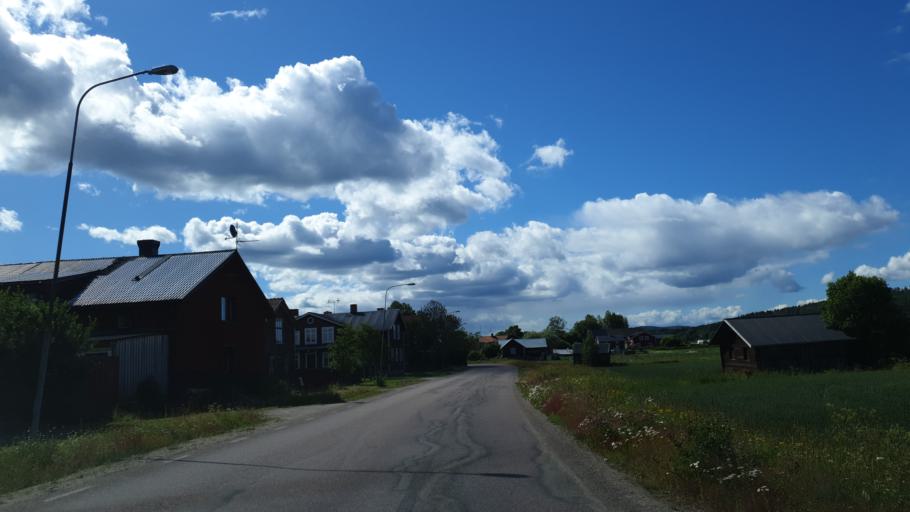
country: SE
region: Gaevleborg
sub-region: Nordanstigs Kommun
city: Bergsjoe
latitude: 62.0490
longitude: 17.2344
